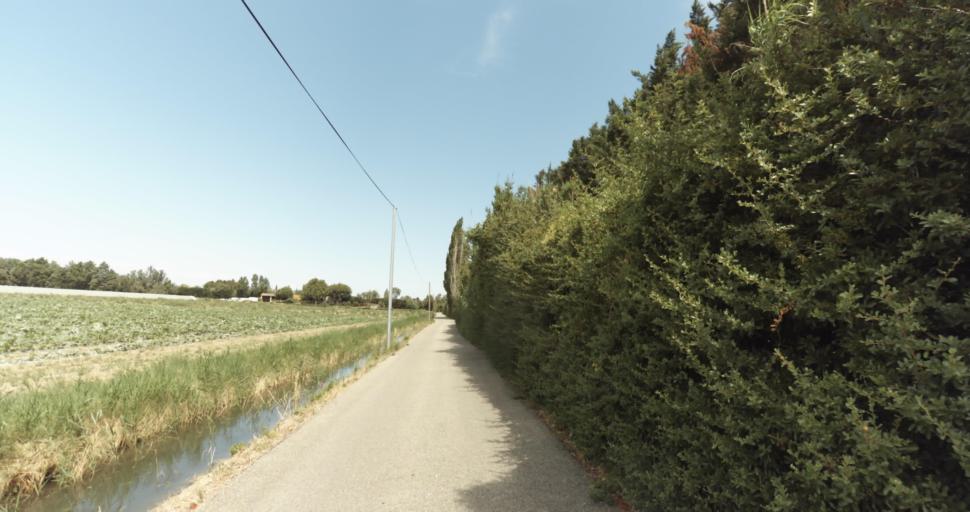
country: FR
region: Provence-Alpes-Cote d'Azur
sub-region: Departement du Vaucluse
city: Althen-des-Paluds
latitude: 44.0342
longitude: 4.9599
